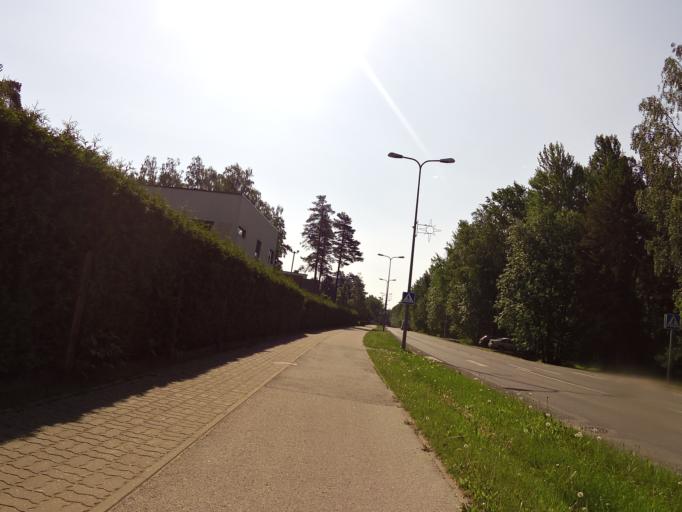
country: EE
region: Harju
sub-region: Harku vald
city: Tabasalu
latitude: 59.4421
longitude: 24.6189
